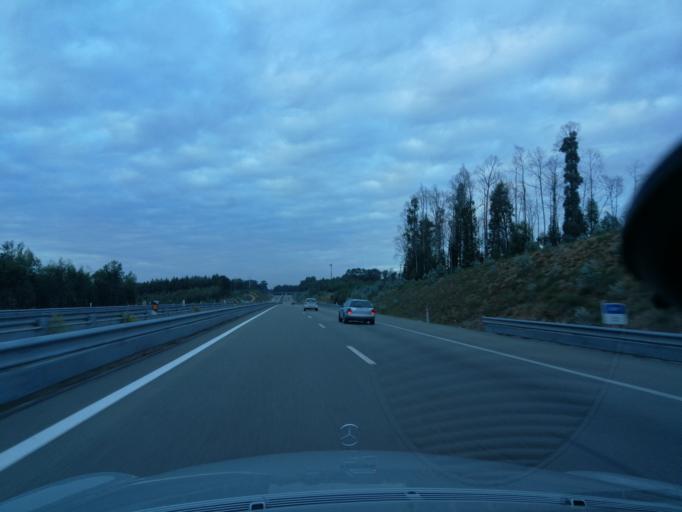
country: PT
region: Aveiro
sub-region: Estarreja
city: Salreu
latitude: 40.7112
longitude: -8.5328
